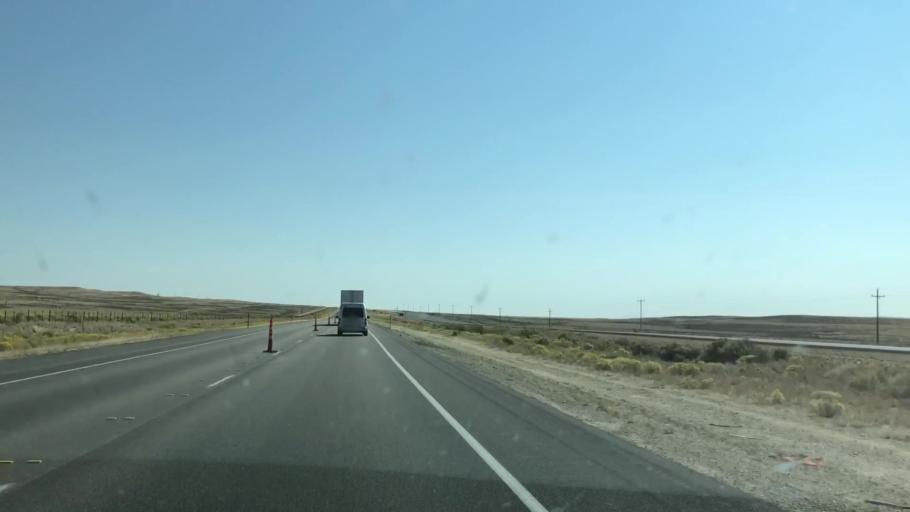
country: US
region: Wyoming
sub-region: Carbon County
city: Rawlins
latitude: 41.7465
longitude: -107.6027
